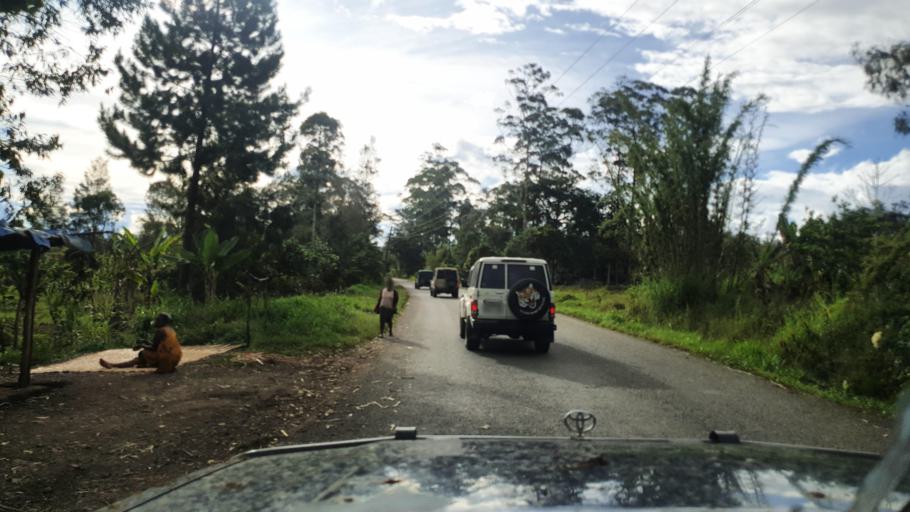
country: PG
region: Jiwaka
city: Minj
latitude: -5.9030
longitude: 144.7511
